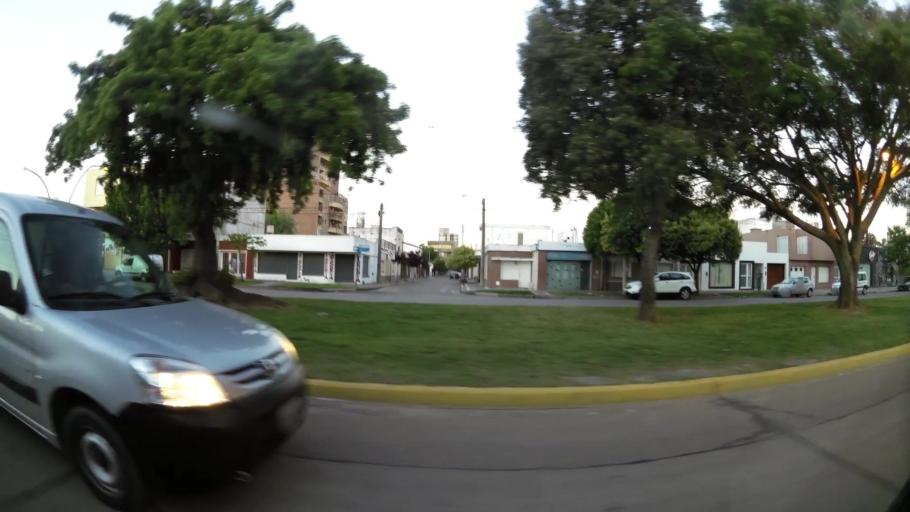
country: AR
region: Cordoba
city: Villa Maria
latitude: -32.4135
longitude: -63.2530
